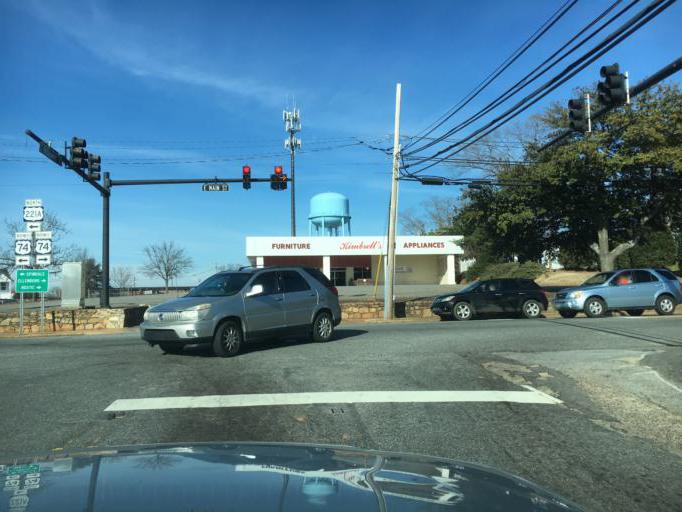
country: US
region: North Carolina
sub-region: Rutherford County
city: Forest City
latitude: 35.3328
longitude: -81.8619
